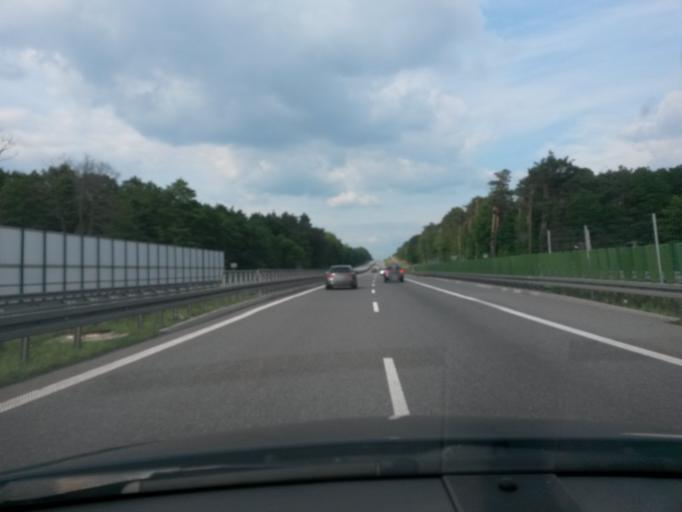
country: PL
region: Lodz Voivodeship
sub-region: Powiat rawski
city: Rawa Mazowiecka
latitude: 51.8272
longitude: 20.3261
